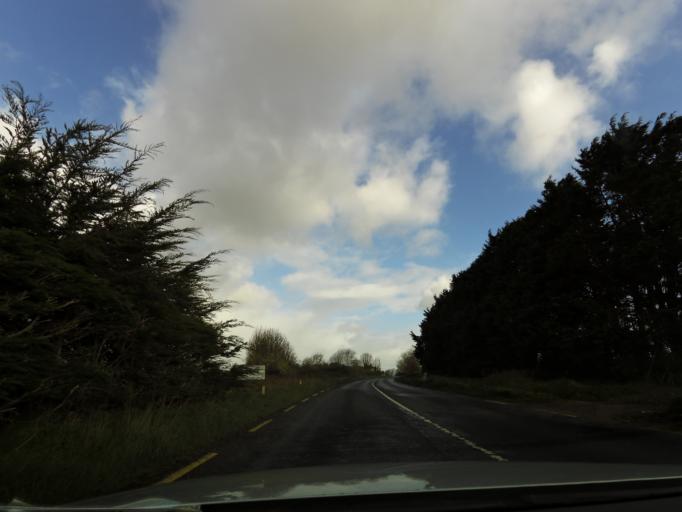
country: IE
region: Munster
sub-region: North Tipperary
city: Nenagh
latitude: 52.8381
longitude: -8.1345
